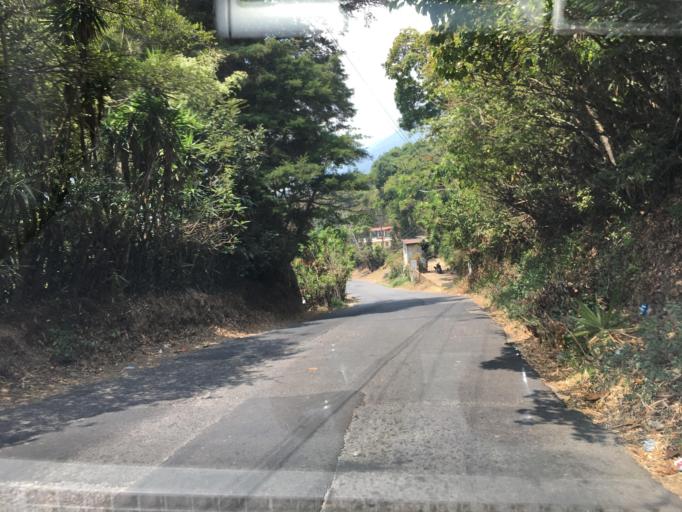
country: GT
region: Guatemala
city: Villa Canales
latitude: 14.3919
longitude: -90.5480
